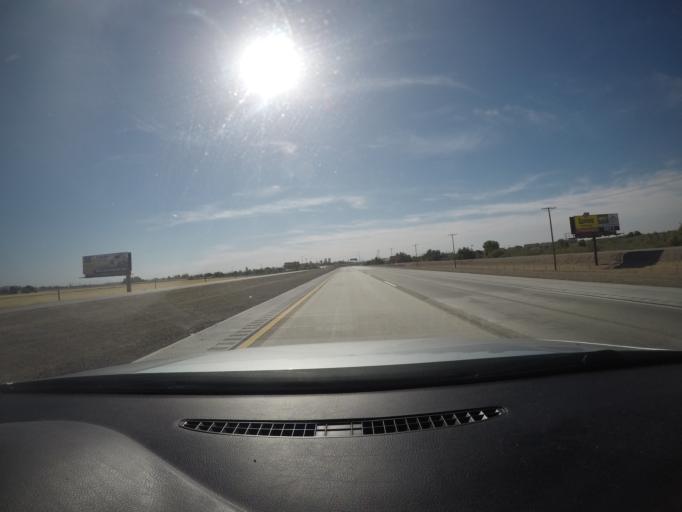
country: US
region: Arizona
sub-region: Yuma County
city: Yuma
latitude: 32.7331
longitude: -114.6316
